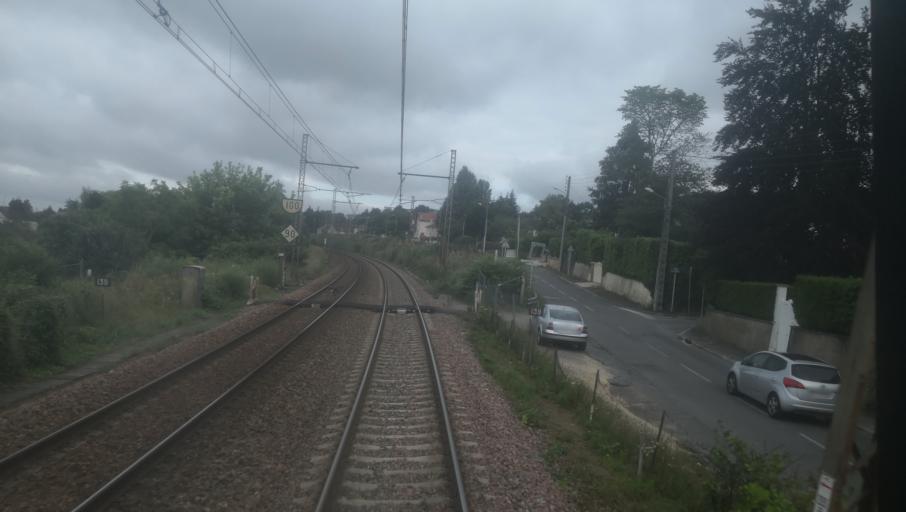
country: FR
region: Centre
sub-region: Departement du Cher
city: Vierzon
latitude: 47.2202
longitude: 2.0889
